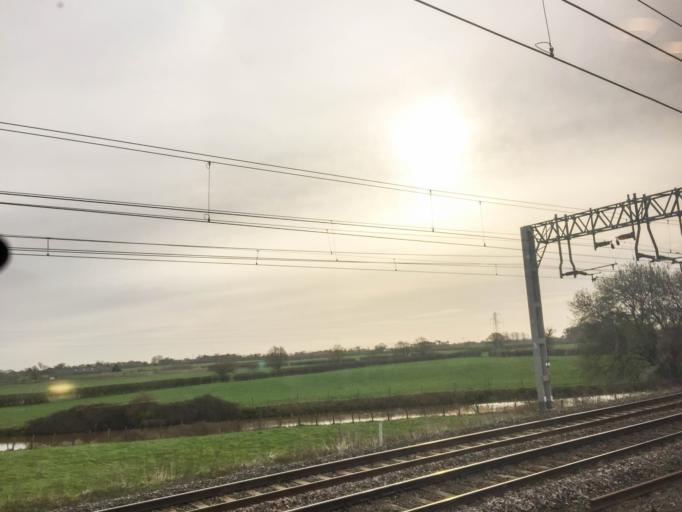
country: GB
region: England
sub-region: Cheshire West and Chester
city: Winsford
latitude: 53.1775
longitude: -2.4836
